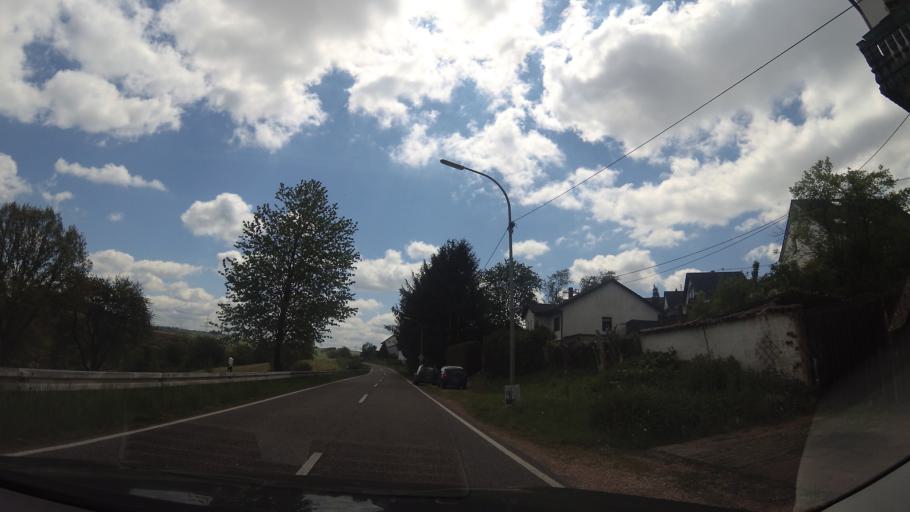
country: DE
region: Saarland
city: Lebach
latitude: 49.4208
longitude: 6.9209
